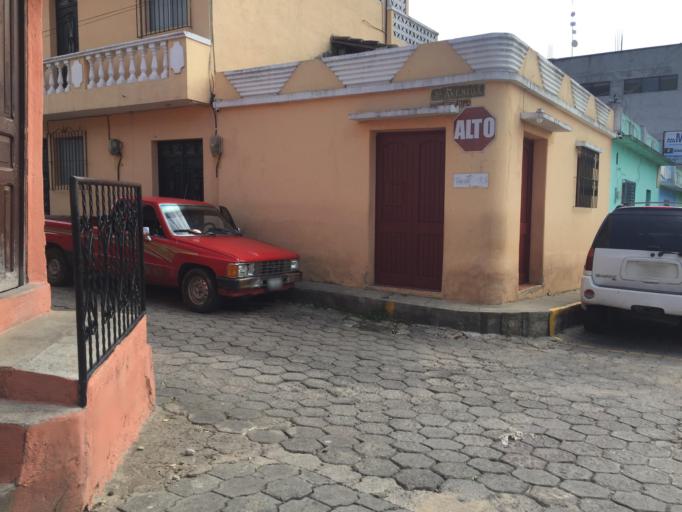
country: GT
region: Totonicapan
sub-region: Municipio de Totonicapan
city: Totonicapan
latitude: 14.9109
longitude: -91.3589
